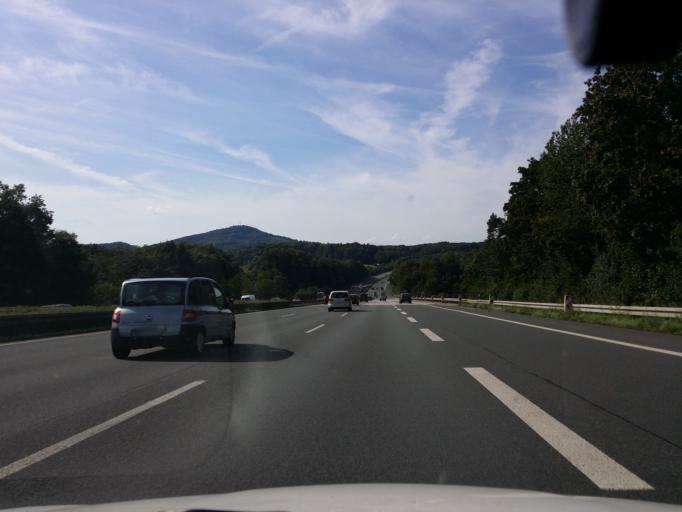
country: DE
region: Rheinland-Pfalz
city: Windhagen
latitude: 50.6757
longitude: 7.2932
